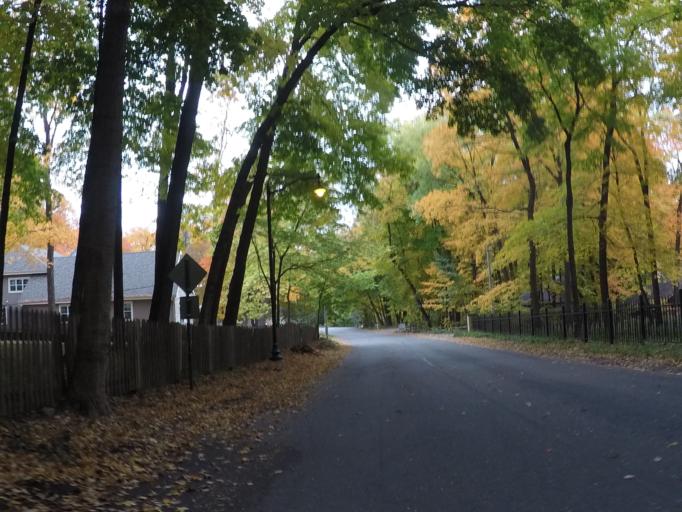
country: US
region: Wisconsin
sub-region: Dane County
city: Maple Bluff
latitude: 43.1146
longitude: -89.3799
